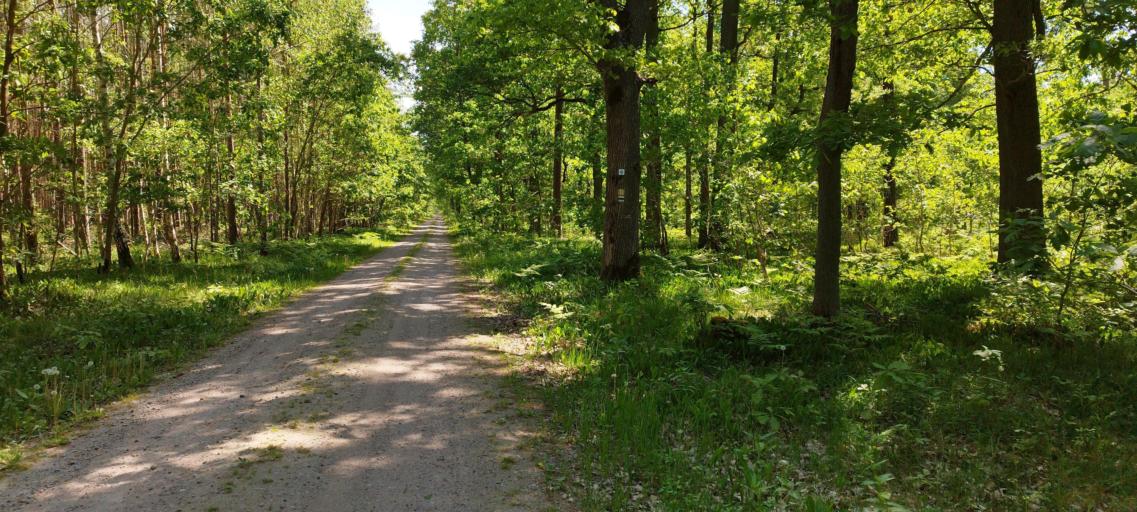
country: DE
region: Brandenburg
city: Spreenhagen
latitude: 52.3943
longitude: 13.9539
